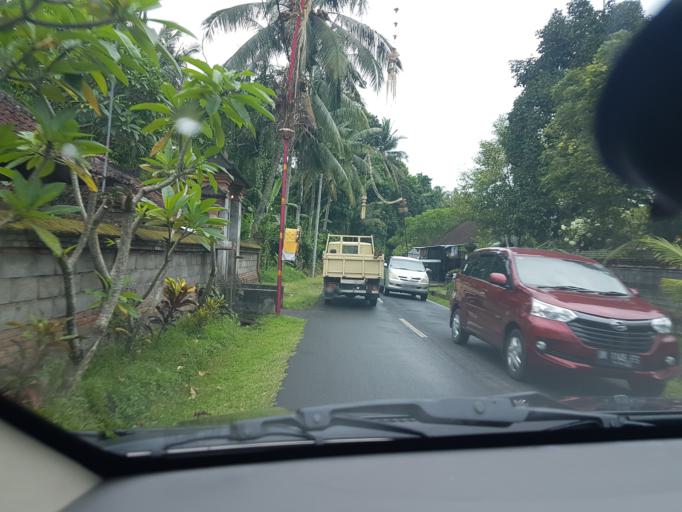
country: ID
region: Bali
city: Banjar Tebongkang
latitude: -8.5273
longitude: 115.2391
